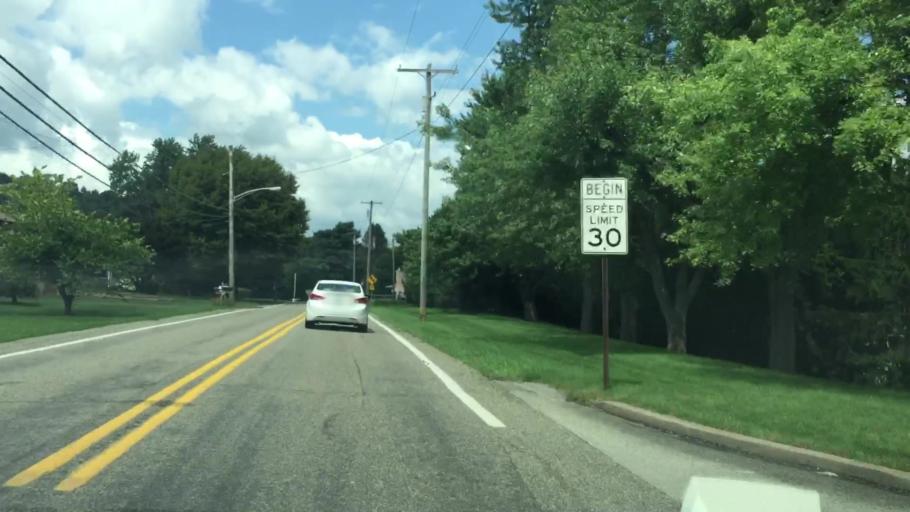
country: US
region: Pennsylvania
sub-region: Allegheny County
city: Cheswick
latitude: 40.5520
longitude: -79.8053
